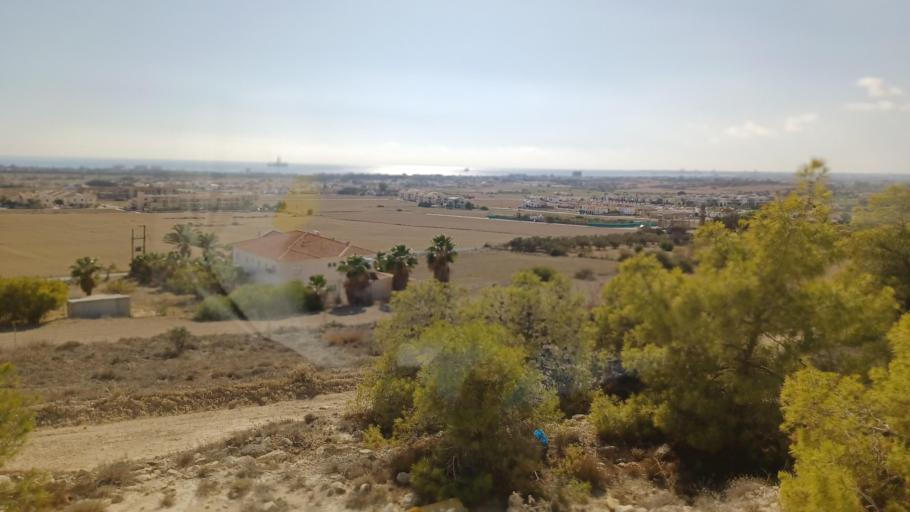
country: CY
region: Larnaka
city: Pyla
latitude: 35.0018
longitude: 33.6775
